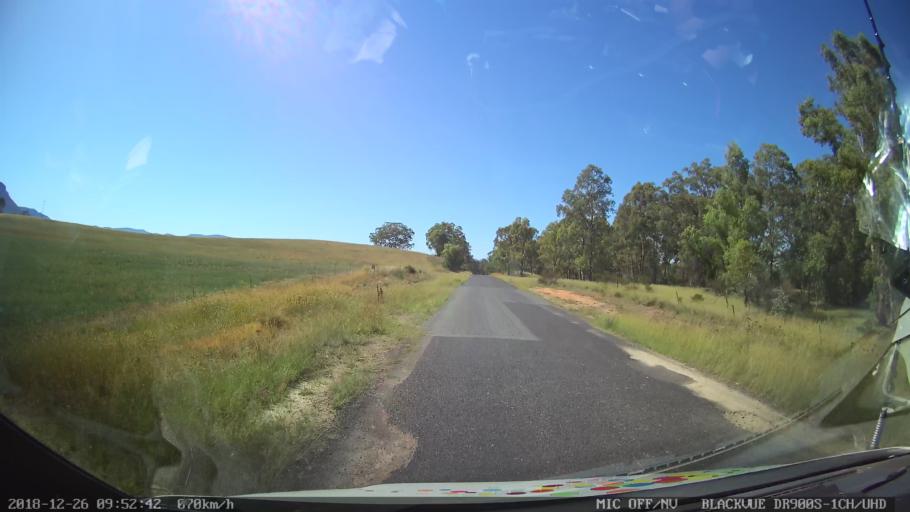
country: AU
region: New South Wales
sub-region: Mid-Western Regional
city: Kandos
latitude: -33.0134
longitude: 150.1500
